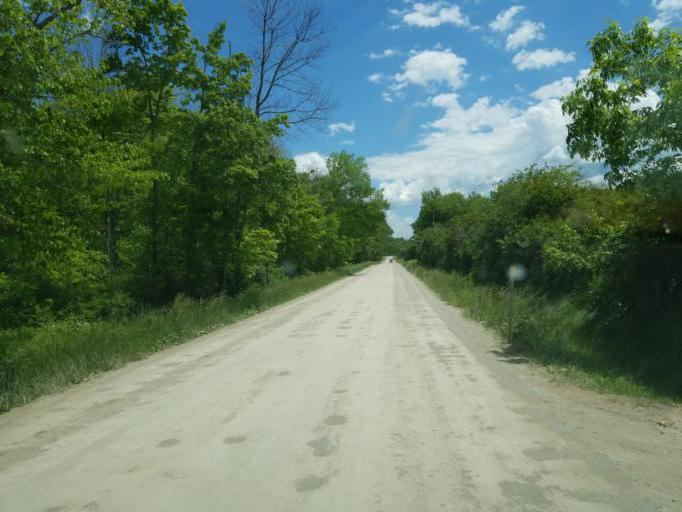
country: US
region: Ohio
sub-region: Geauga County
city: Middlefield
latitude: 41.3863
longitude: -81.0684
